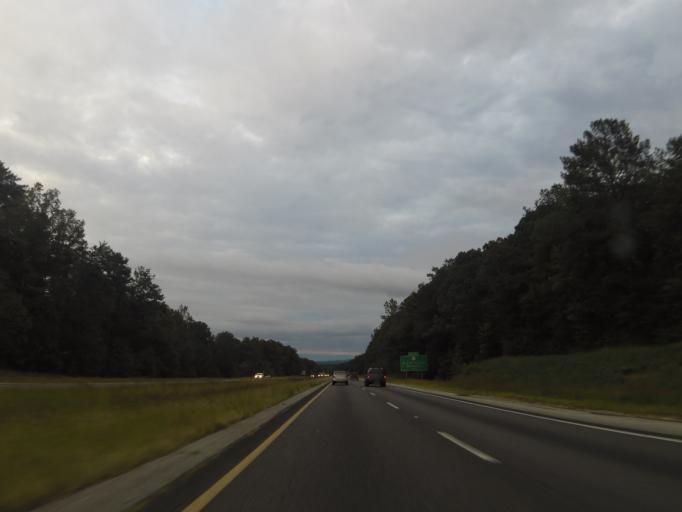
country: US
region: Alabama
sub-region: Saint Clair County
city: Springville
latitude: 33.7725
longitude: -86.4493
